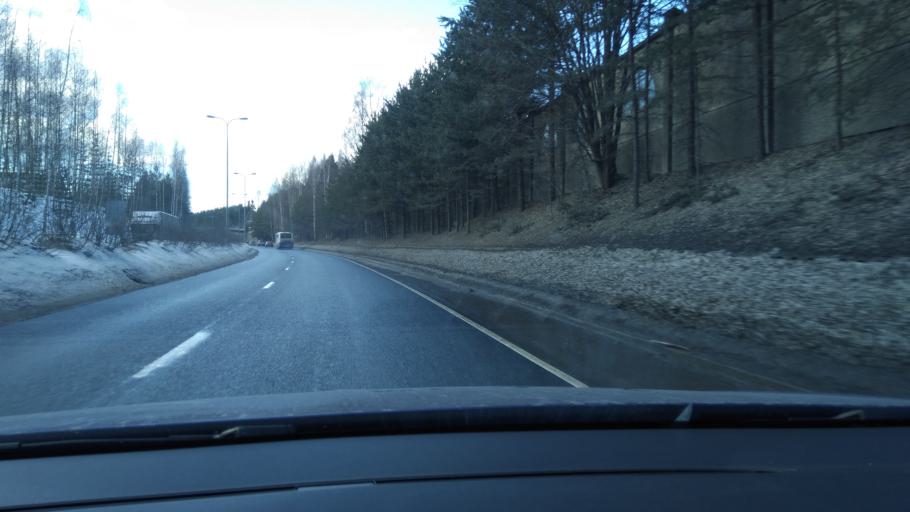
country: FI
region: Pirkanmaa
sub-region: Tampere
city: Tampere
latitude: 61.5048
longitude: 23.8001
